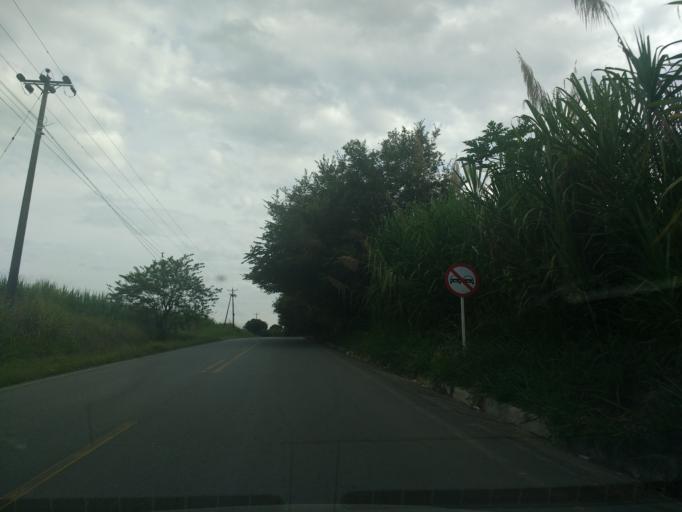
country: CO
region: Valle del Cauca
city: Florida
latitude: 3.2899
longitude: -76.2269
